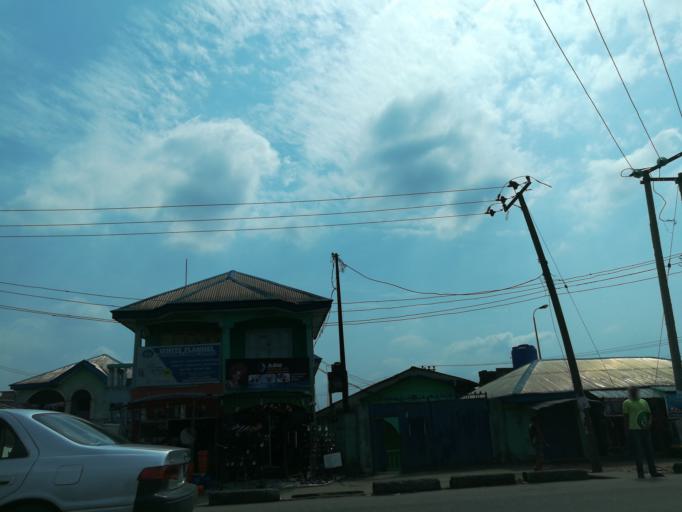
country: NG
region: Rivers
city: Port Harcourt
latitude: 4.8277
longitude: 6.9814
